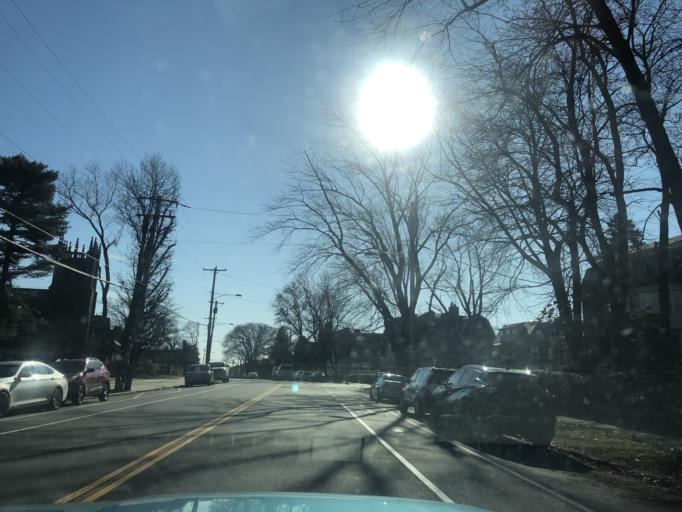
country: US
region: Pennsylvania
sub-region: Montgomery County
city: Bala-Cynwyd
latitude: 39.9912
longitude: -75.2336
